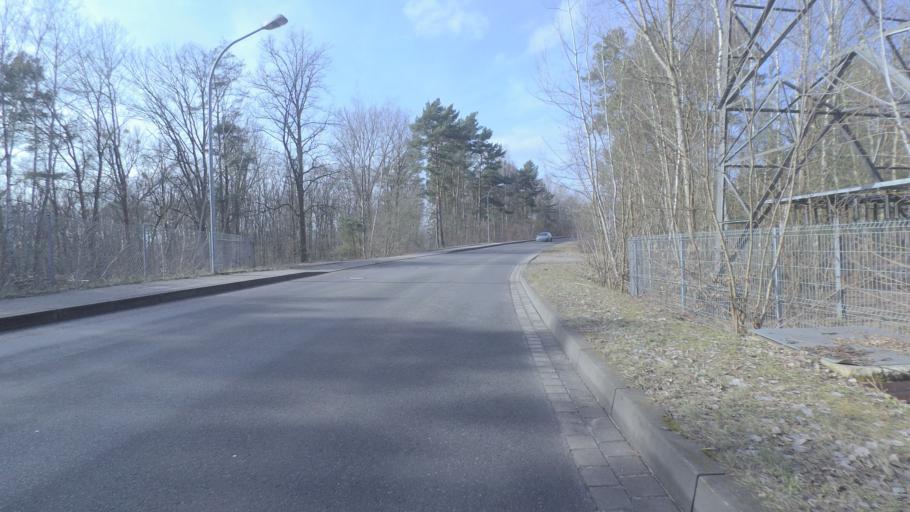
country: DE
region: Brandenburg
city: Ludwigsfelde
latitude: 52.3047
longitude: 13.2723
